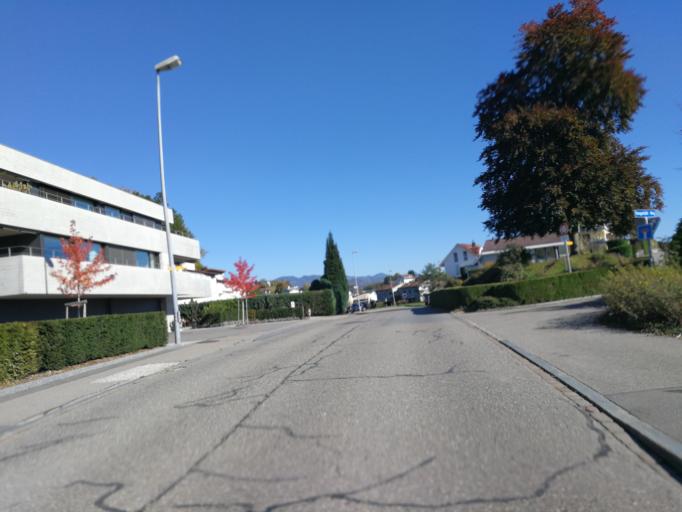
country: CH
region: Saint Gallen
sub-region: Wahlkreis See-Gaster
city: Rapperswil
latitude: 47.2427
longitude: 8.8135
